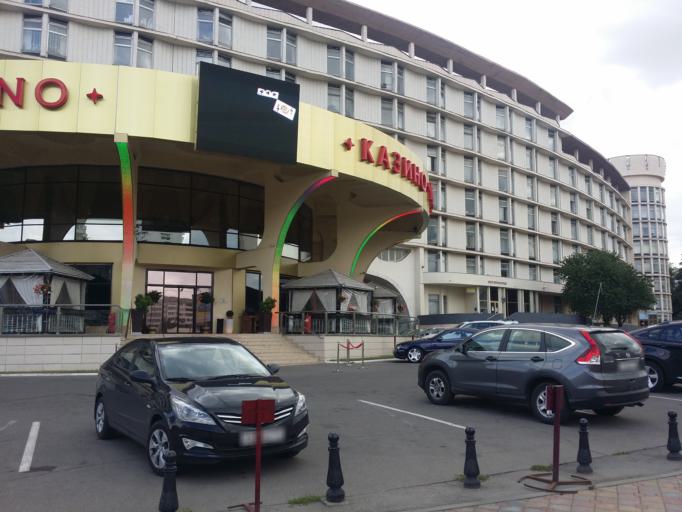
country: BY
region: Minsk
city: Minsk
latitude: 53.9164
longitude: 27.5645
